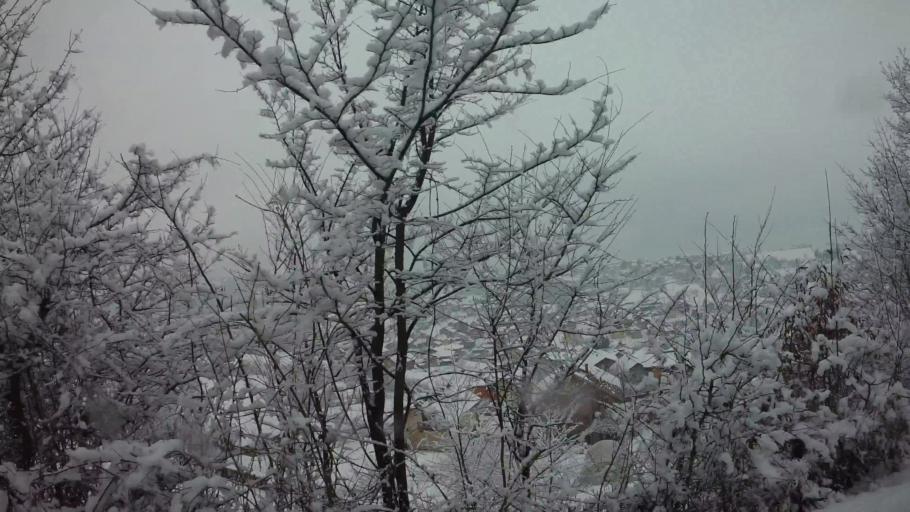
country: BA
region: Federation of Bosnia and Herzegovina
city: Vogosca
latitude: 43.8772
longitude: 18.3239
